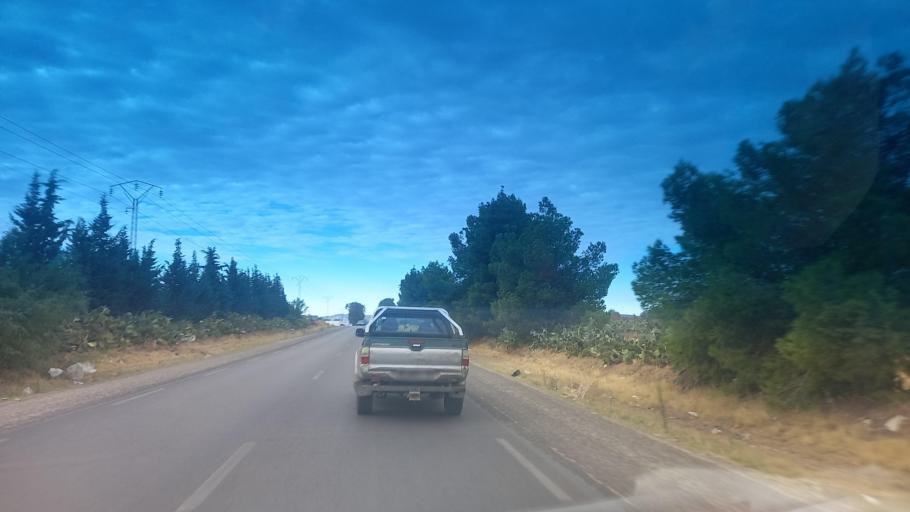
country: TN
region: Al Qasrayn
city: Sbiba
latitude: 35.2756
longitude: 9.0936
